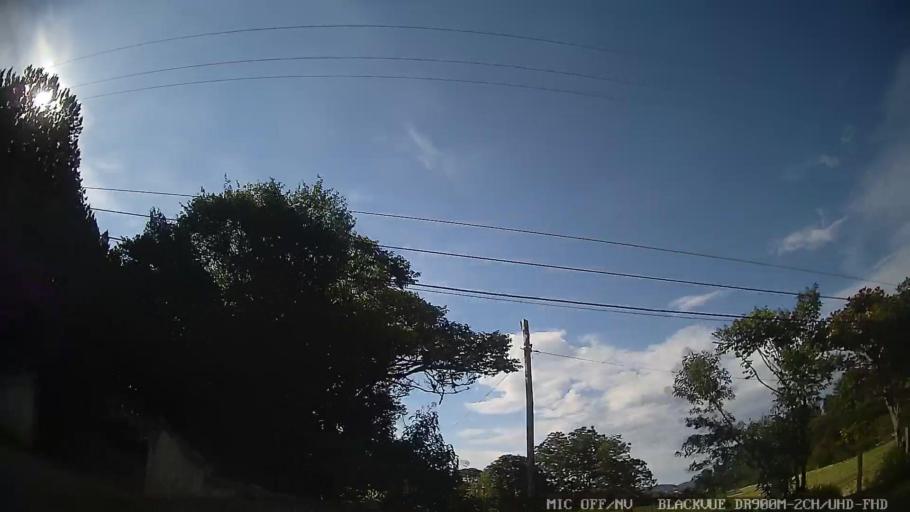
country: BR
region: Sao Paulo
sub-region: Serra Negra
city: Serra Negra
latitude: -22.6419
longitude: -46.6957
